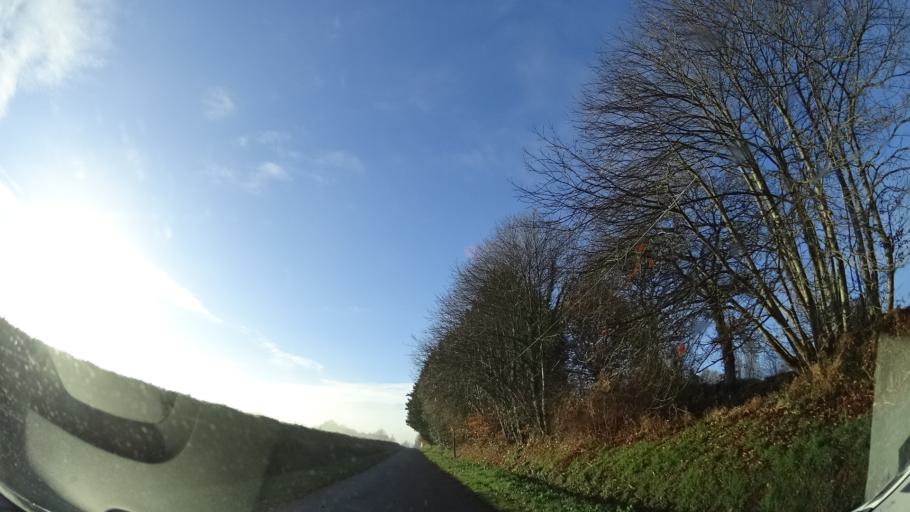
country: FR
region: Brittany
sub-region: Departement d'Ille-et-Vilaine
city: Montgermont
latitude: 48.1839
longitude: -1.6963
